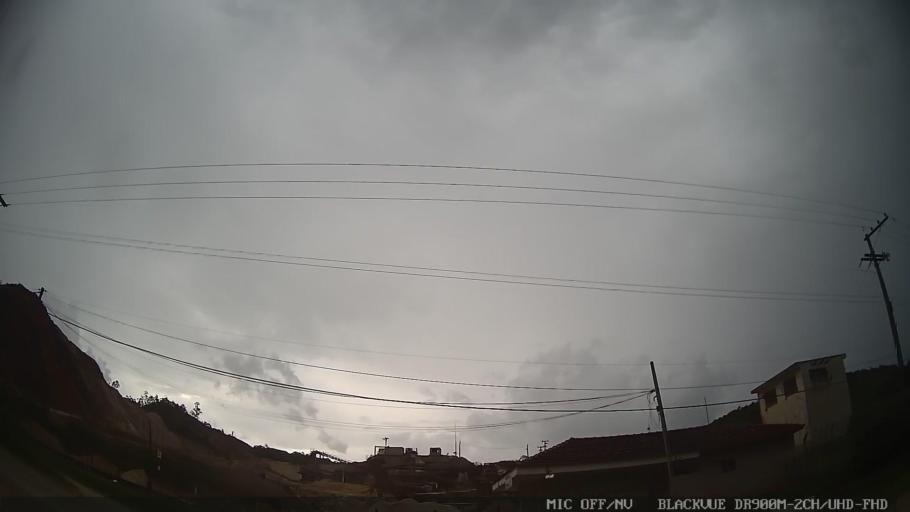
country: BR
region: Sao Paulo
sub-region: Pedreira
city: Pedreira
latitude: -22.7099
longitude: -46.8648
